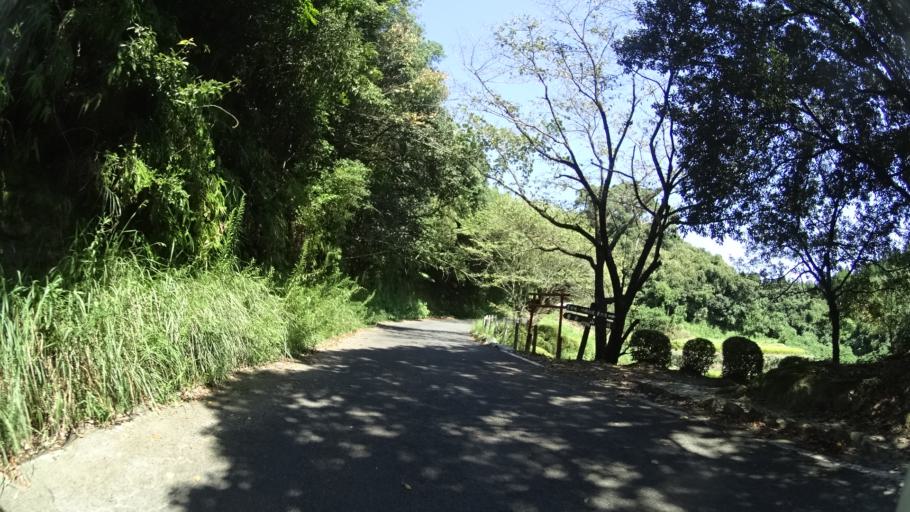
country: JP
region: Kagoshima
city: Kajiki
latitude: 31.7529
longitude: 130.6694
